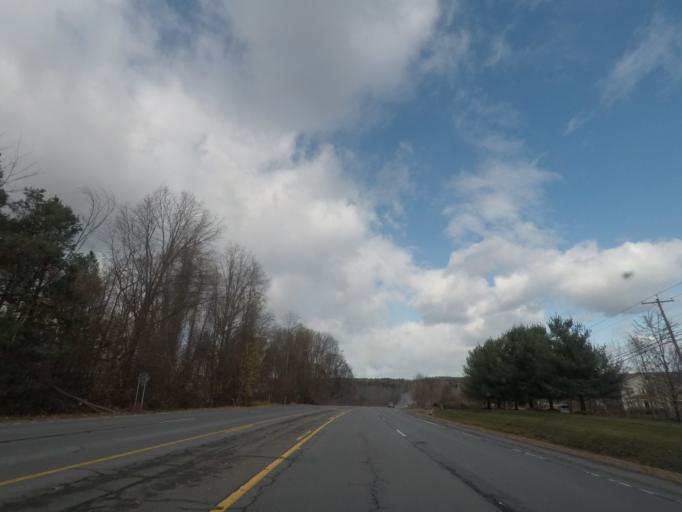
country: US
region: New York
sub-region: Saratoga County
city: Ballston Spa
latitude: 42.9964
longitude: -73.7911
